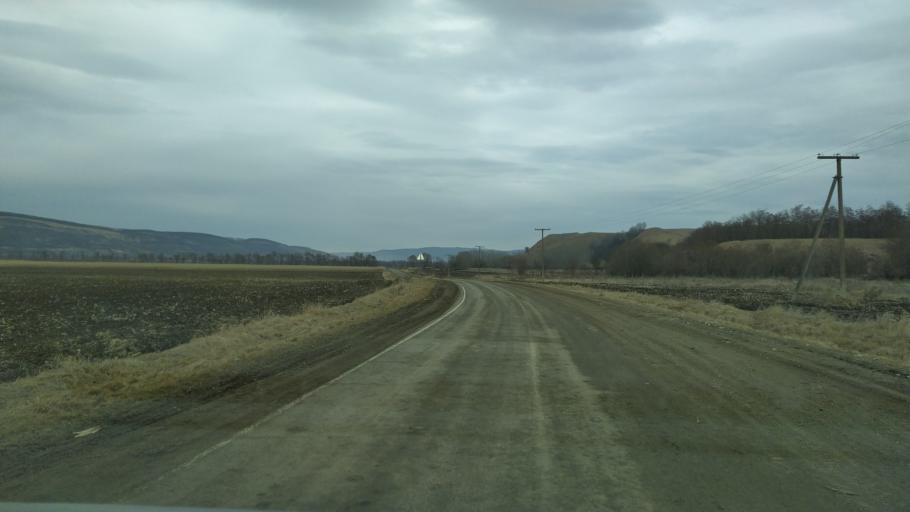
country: RU
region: Krasnodarskiy
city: Peredovaya
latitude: 44.1005
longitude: 41.4080
